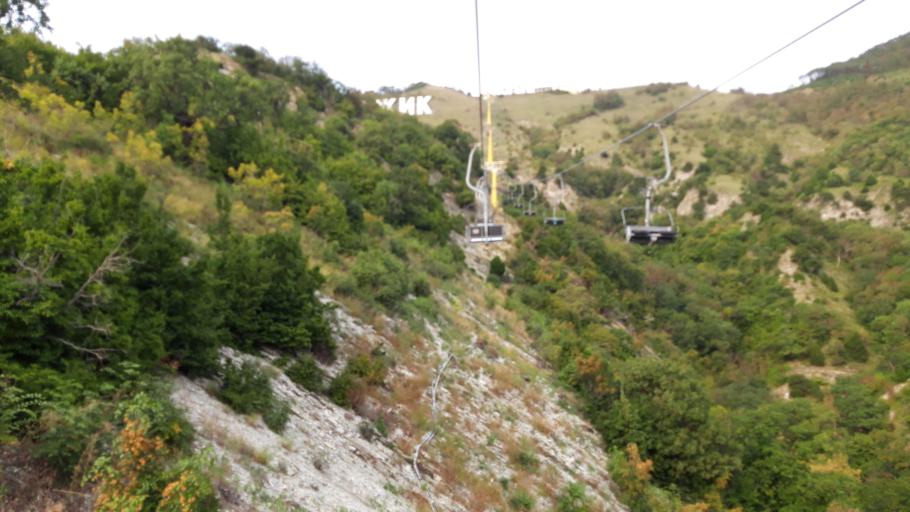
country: RU
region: Krasnodarskiy
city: Gelendzhik
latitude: 44.5809
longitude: 38.0967
